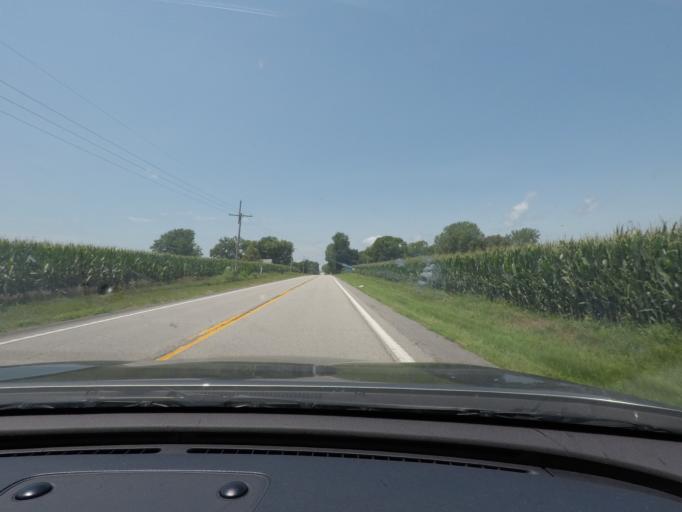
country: US
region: Missouri
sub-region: Saline County
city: Marshall
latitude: 39.1930
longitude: -93.3516
